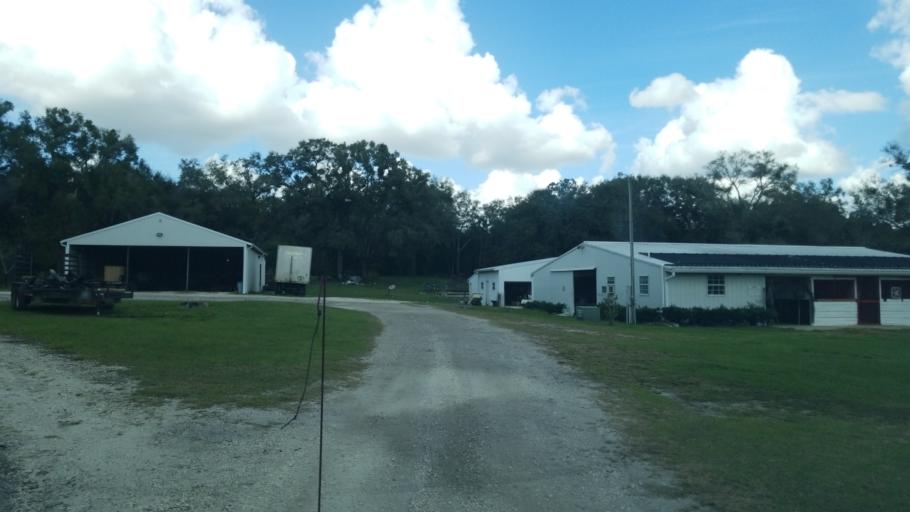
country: US
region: Florida
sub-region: Marion County
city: Ocala
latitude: 29.1555
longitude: -82.2583
